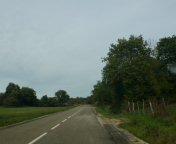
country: FR
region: Bourgogne
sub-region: Departement de Saone-et-Loire
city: Cuiseaux
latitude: 46.4585
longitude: 5.4345
